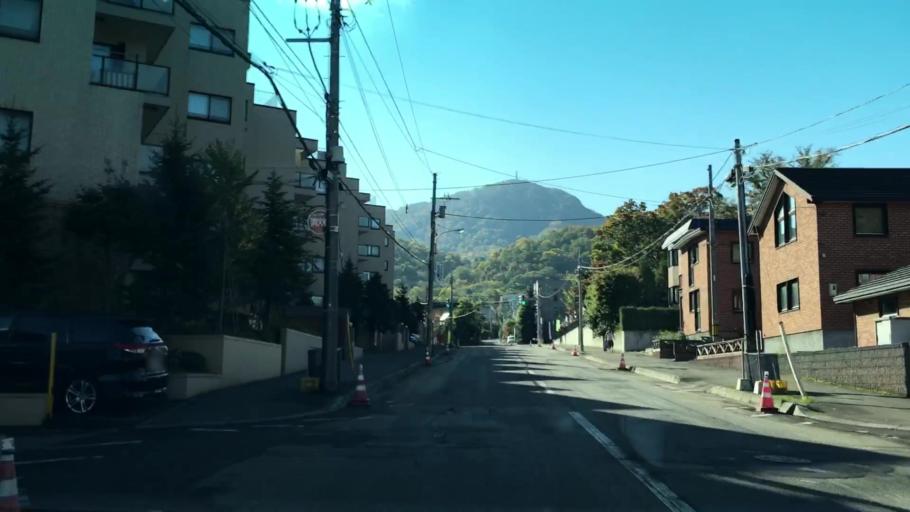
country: JP
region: Hokkaido
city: Sapporo
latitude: 43.0417
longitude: 141.3200
